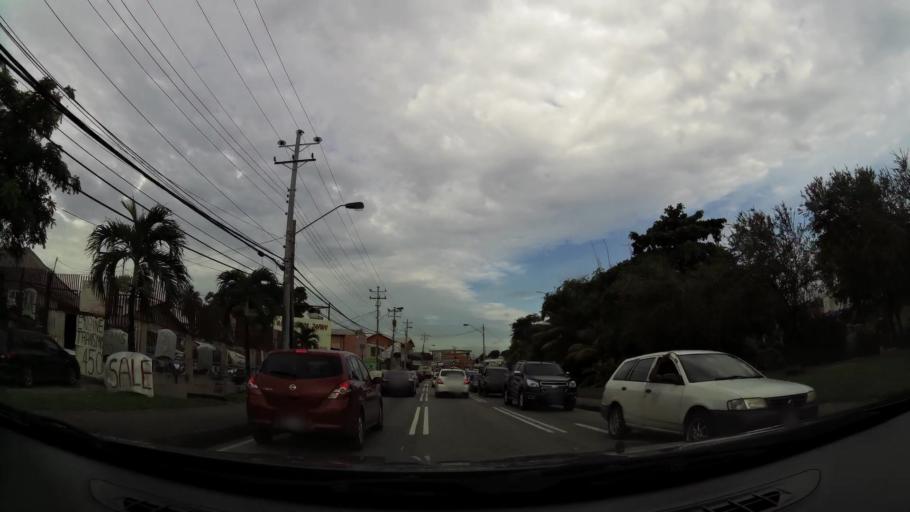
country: TT
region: Tunapuna/Piarco
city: Tunapuna
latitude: 10.6503
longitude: -61.4356
